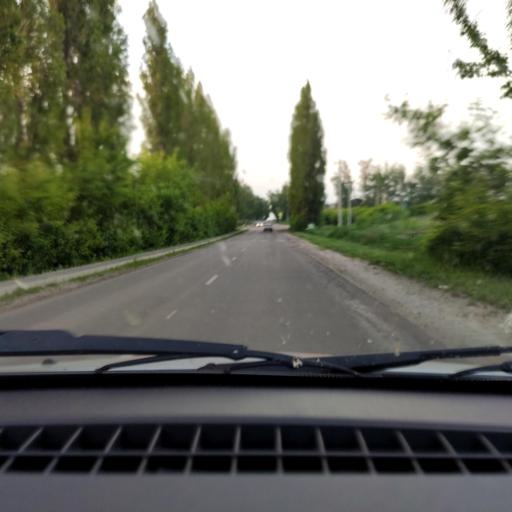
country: RU
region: Voronezj
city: Ramon'
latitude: 51.9364
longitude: 39.3484
